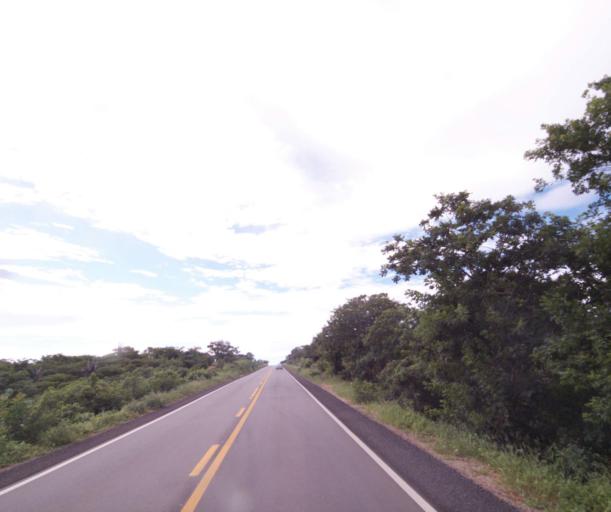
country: BR
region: Bahia
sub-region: Guanambi
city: Guanambi
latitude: -14.4077
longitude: -42.7424
